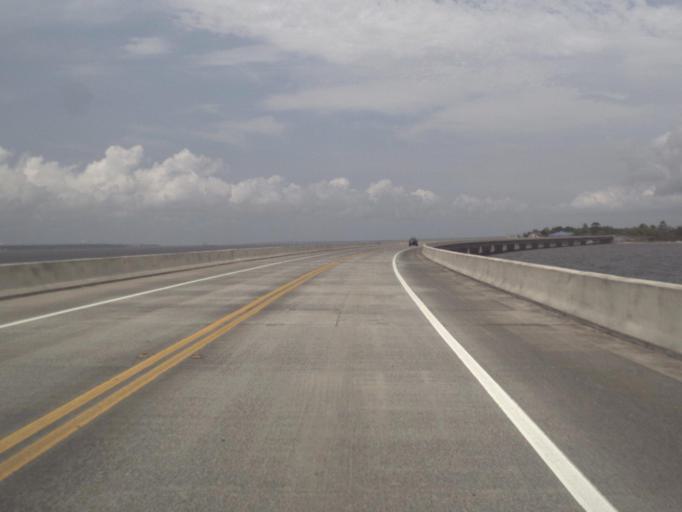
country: US
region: Florida
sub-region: Santa Rosa County
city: Oriole Beach
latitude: 30.4361
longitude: -87.0989
